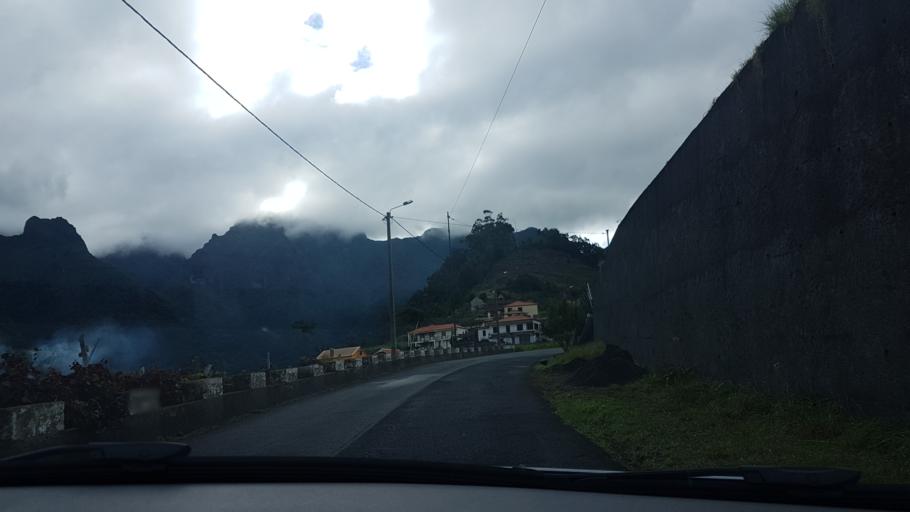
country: PT
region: Madeira
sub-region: Sao Vicente
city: Sao Vicente
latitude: 32.7809
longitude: -17.0297
